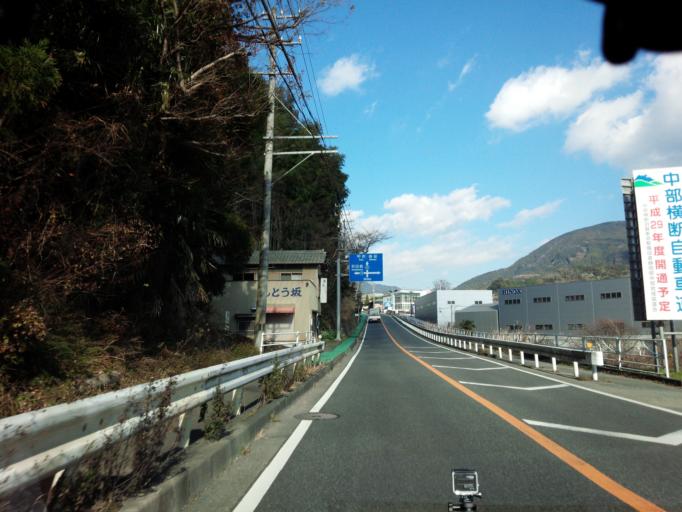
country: JP
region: Shizuoka
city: Fujinomiya
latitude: 35.0945
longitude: 138.5134
